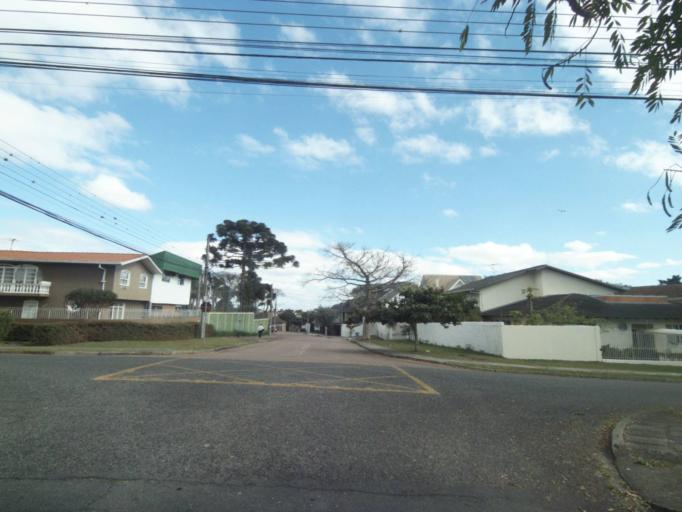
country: BR
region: Parana
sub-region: Curitiba
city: Curitiba
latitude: -25.4563
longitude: -49.2733
